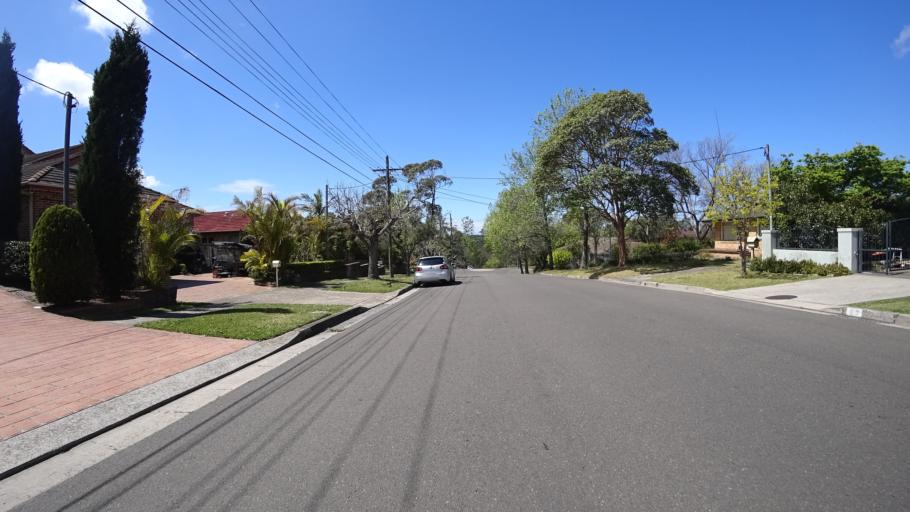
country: AU
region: New South Wales
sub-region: Warringah
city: Forestville
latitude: -33.7648
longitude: 151.2178
